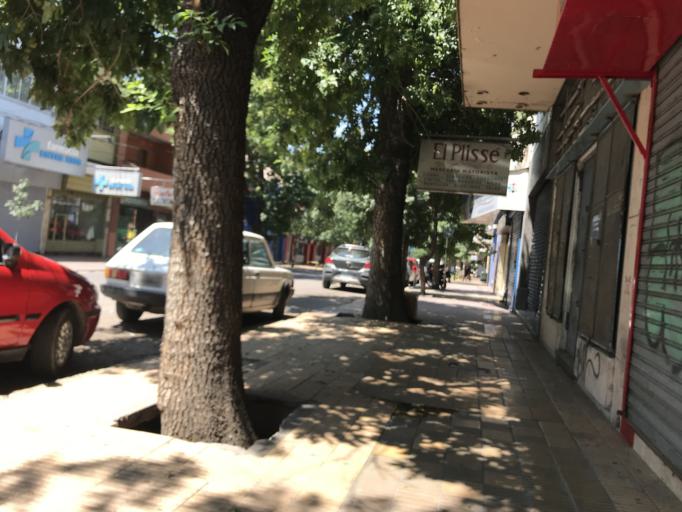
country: AR
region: Mendoza
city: Mendoza
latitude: -32.8861
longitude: -68.8367
